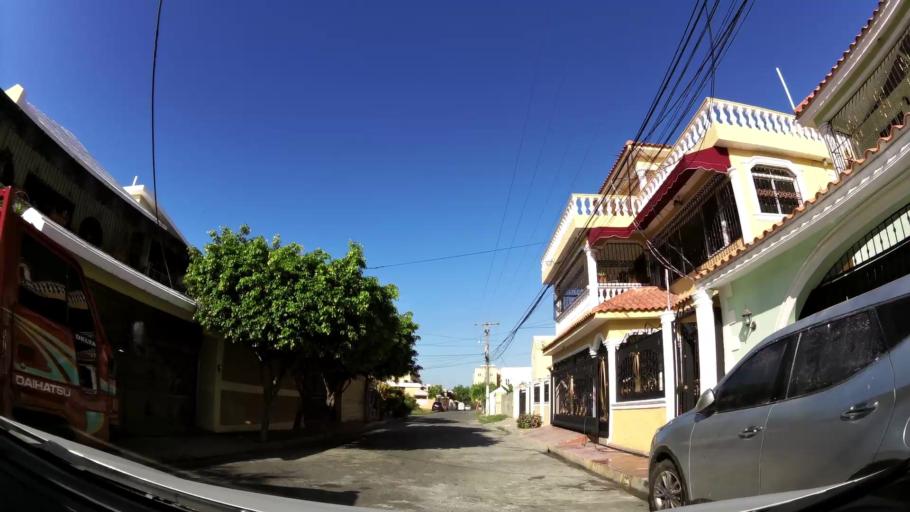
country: DO
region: Santo Domingo
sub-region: Santo Domingo
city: Santo Domingo Este
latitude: 18.4713
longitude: -69.8606
